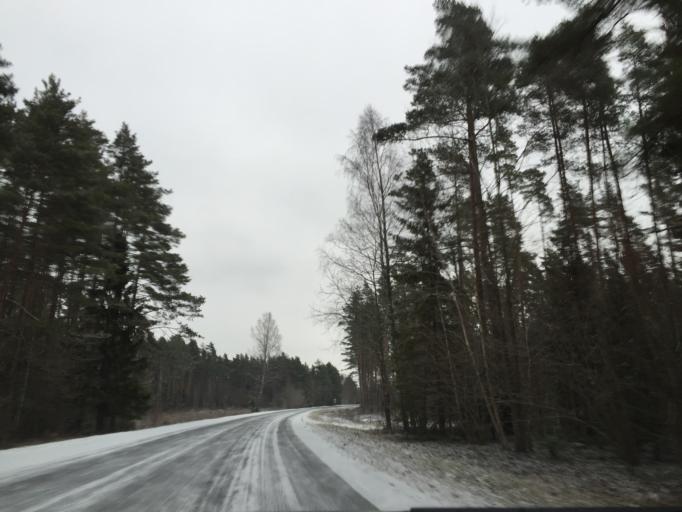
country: EE
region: Saare
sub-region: Orissaare vald
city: Orissaare
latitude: 58.5986
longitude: 23.1668
